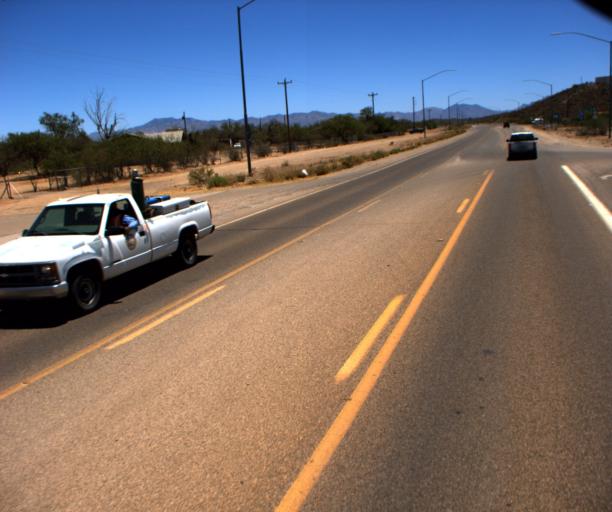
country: US
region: Arizona
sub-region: Pima County
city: Sells
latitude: 31.9222
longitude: -111.8928
